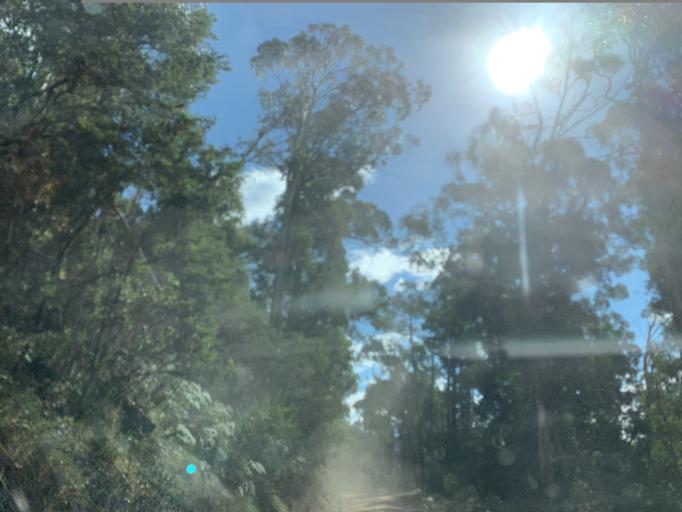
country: AU
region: Victoria
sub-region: Mansfield
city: Mansfield
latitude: -37.0990
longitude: 146.5093
